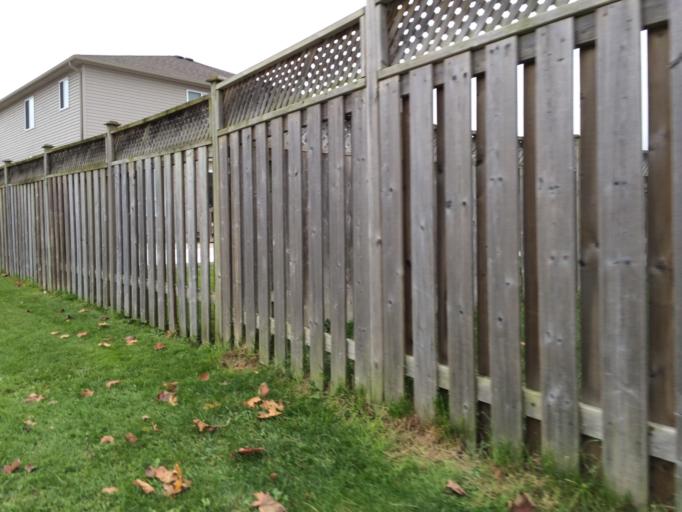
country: CA
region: Ontario
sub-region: Wellington County
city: Guelph
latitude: 43.5239
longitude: -80.3007
